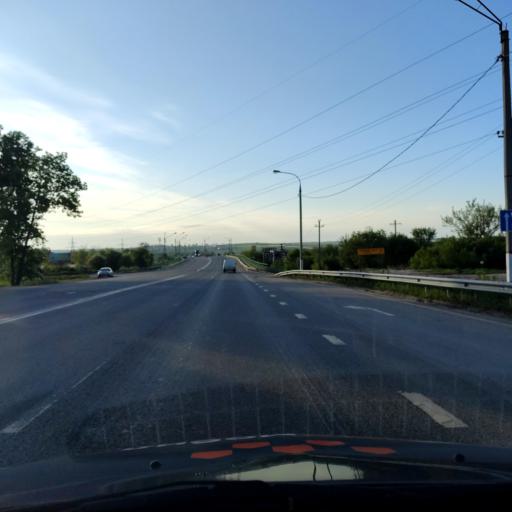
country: RU
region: Lipetsk
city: Yelets
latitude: 52.5927
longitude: 38.4889
